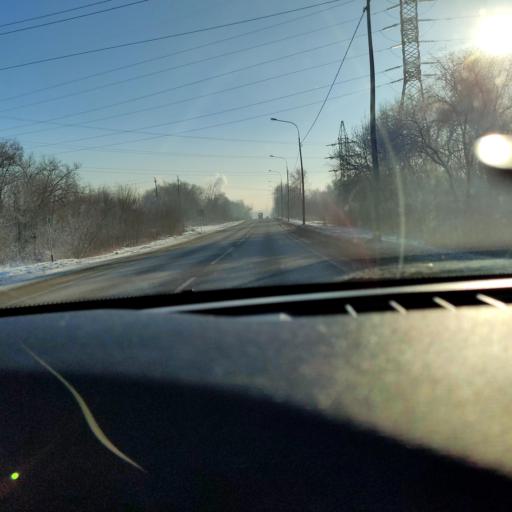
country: RU
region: Samara
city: Petra-Dubrava
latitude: 53.2753
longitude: 50.3820
